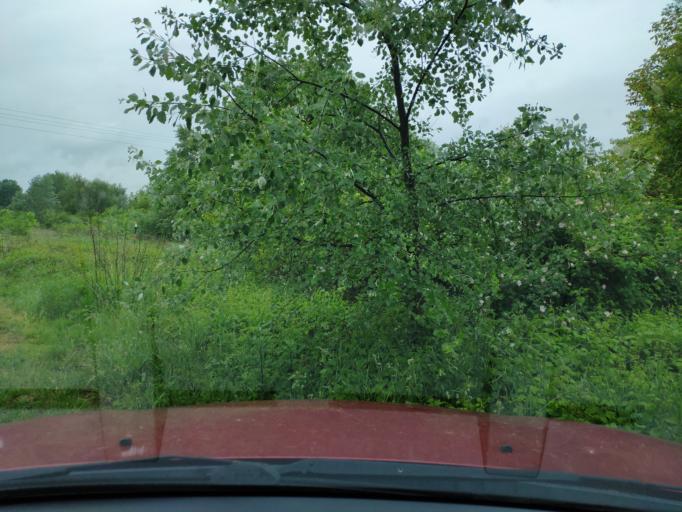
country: SK
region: Kosicky
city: Cierna nad Tisou
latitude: 48.4178
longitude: 22.0569
